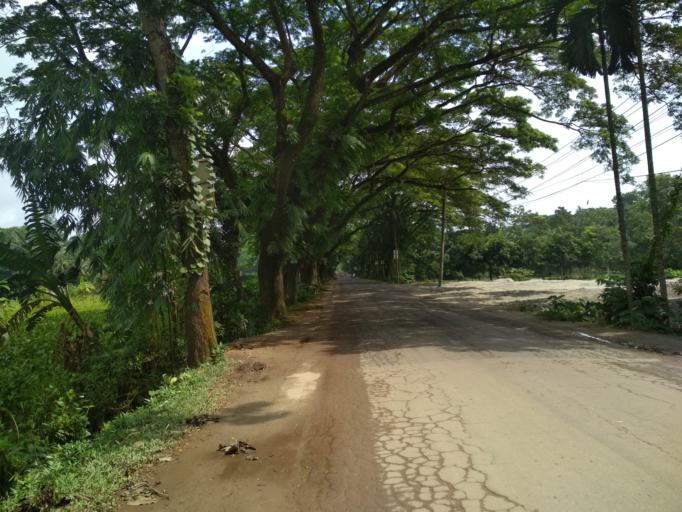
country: BD
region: Chittagong
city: Lakshmipur
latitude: 22.9498
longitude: 90.8087
